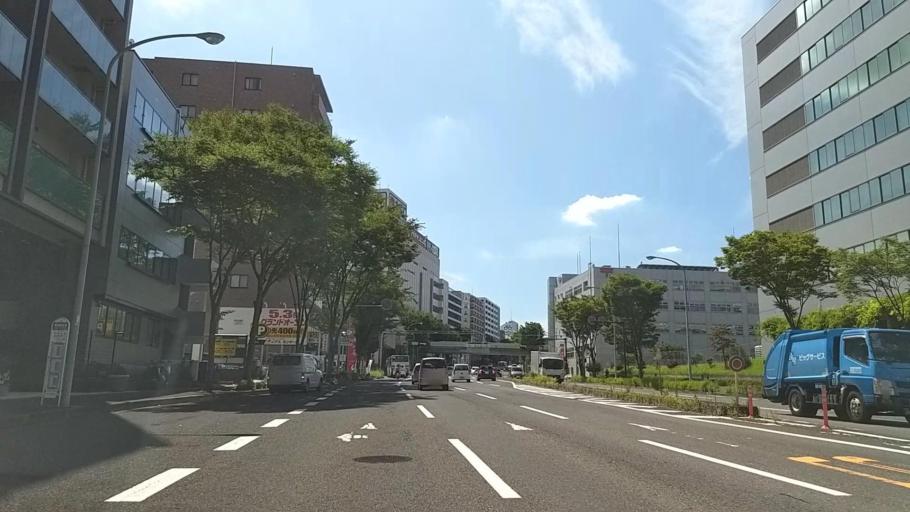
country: JP
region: Tokyo
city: Chofugaoka
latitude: 35.5466
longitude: 139.5729
